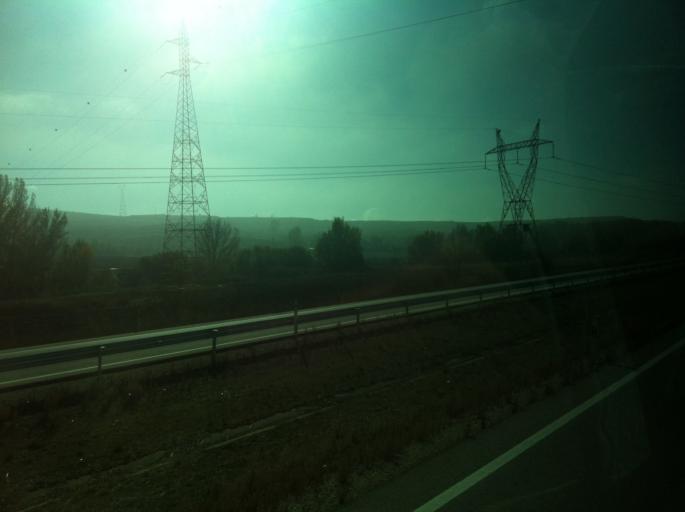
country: ES
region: Castille and Leon
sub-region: Provincia de Burgos
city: Rubena
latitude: 42.3975
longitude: -3.5664
